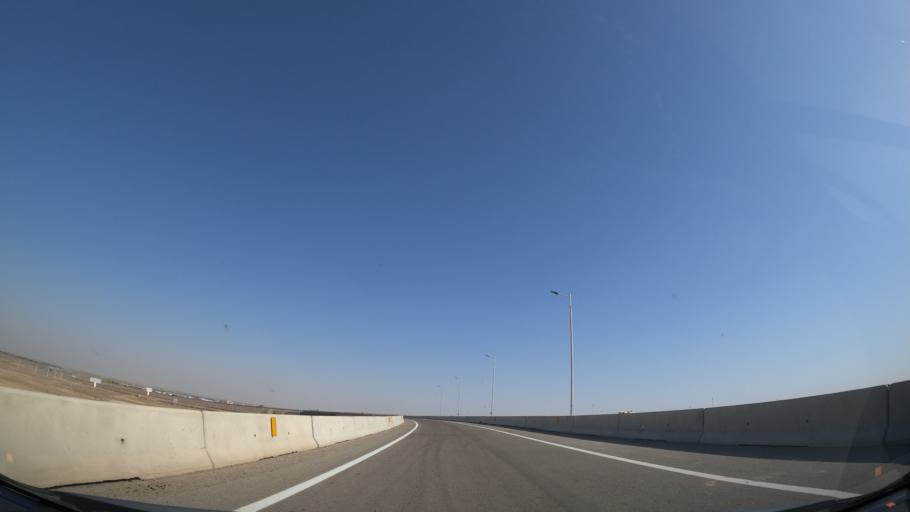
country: IR
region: Tehran
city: Eqbaliyeh
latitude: 35.1334
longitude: 51.5107
